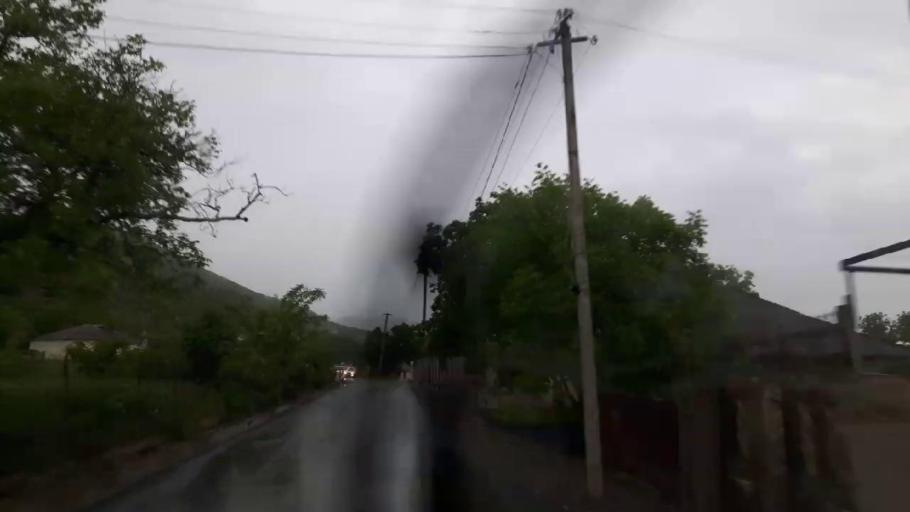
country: GE
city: Agara
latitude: 41.9818
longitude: 43.9375
